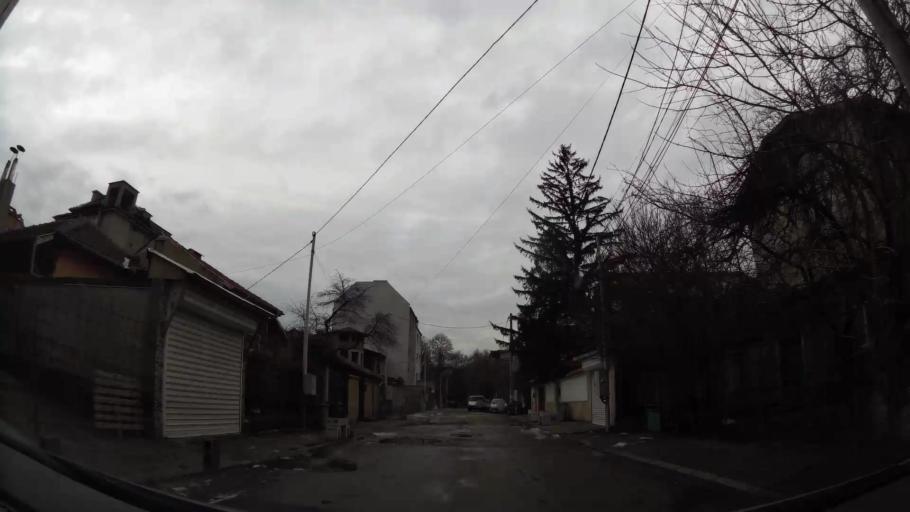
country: BG
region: Sofia-Capital
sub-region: Stolichna Obshtina
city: Sofia
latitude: 42.7220
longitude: 23.3045
